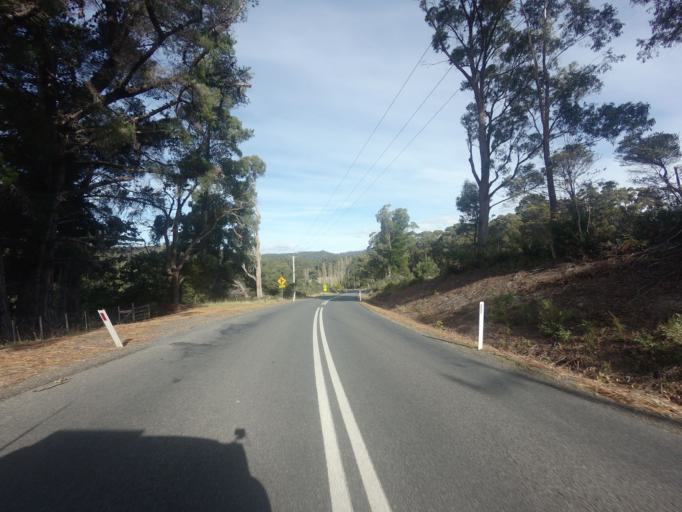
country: AU
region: Tasmania
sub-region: Clarence
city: Sandford
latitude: -43.0615
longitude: 147.8325
